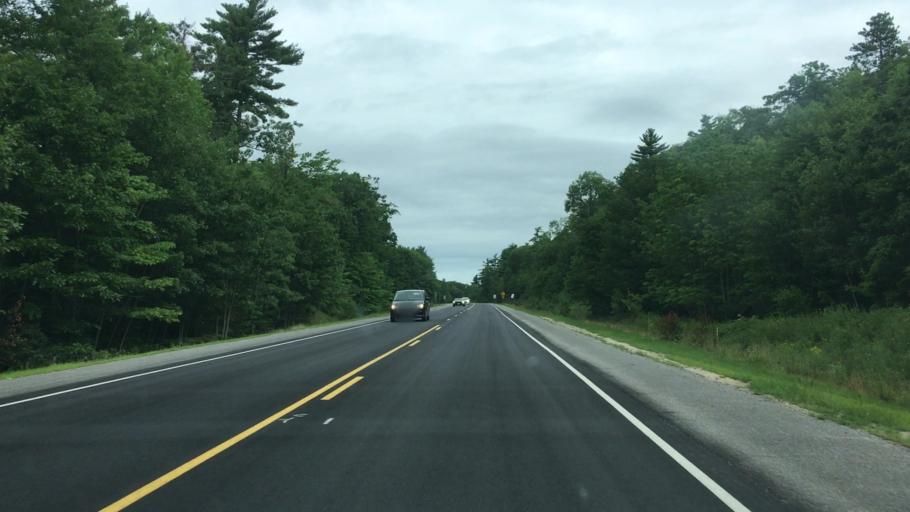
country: US
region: Maine
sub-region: Washington County
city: Cherryfield
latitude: 44.9020
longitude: -67.8561
